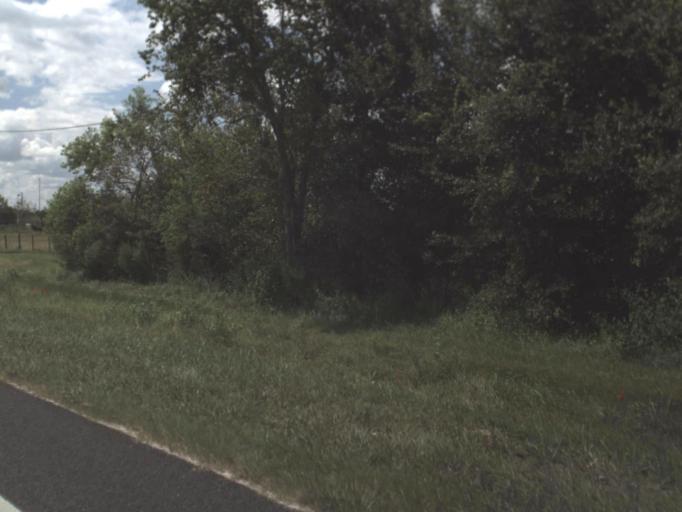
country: US
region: Florida
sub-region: Polk County
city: Wahneta
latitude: 27.9164
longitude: -81.7232
